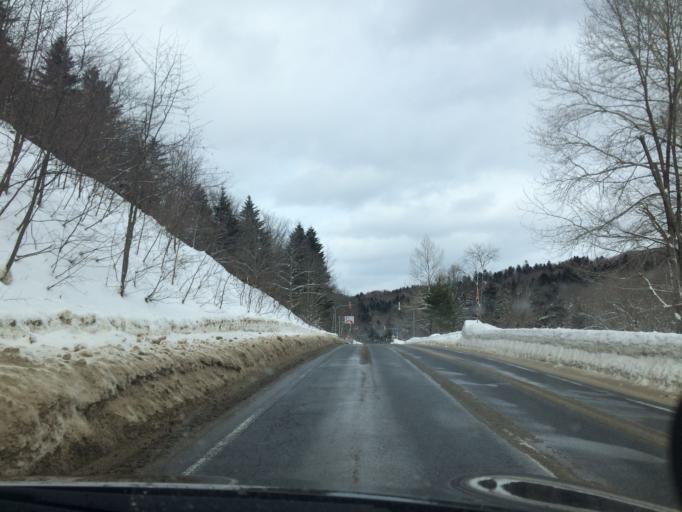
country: JP
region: Hokkaido
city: Shimo-furano
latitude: 42.9127
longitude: 142.3732
